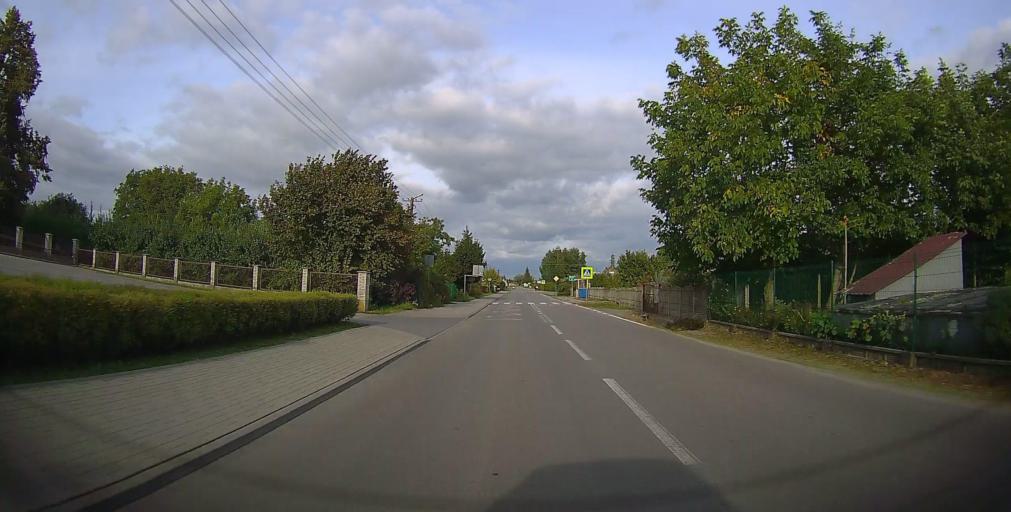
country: PL
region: Masovian Voivodeship
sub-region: Powiat grojecki
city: Jasieniec
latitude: 51.7556
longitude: 20.9586
